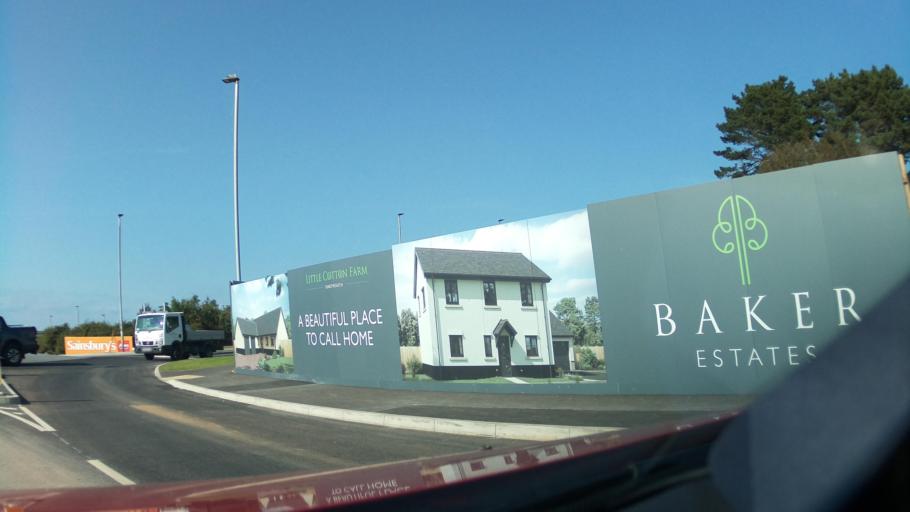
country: GB
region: England
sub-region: Devon
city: Dartmouth
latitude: 50.3458
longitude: -3.6040
